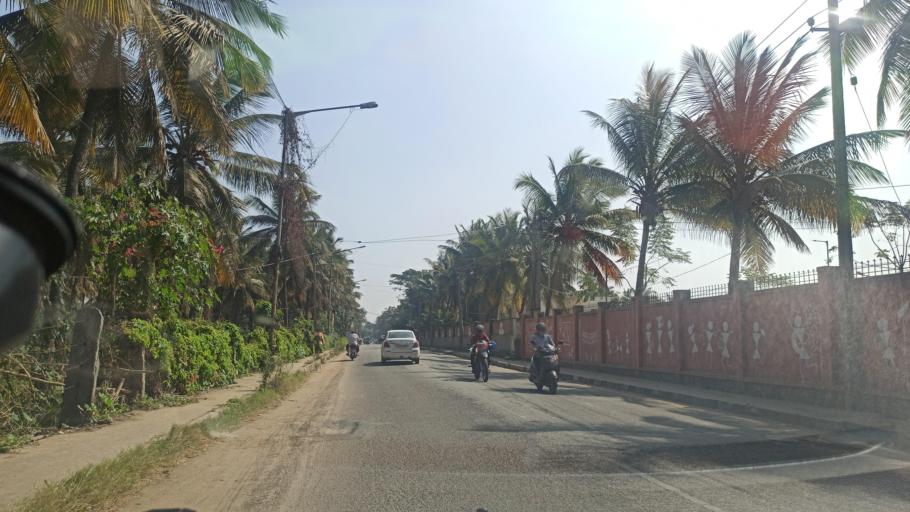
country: IN
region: Karnataka
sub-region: Bangalore Urban
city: Yelahanka
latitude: 13.0419
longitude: 77.5843
